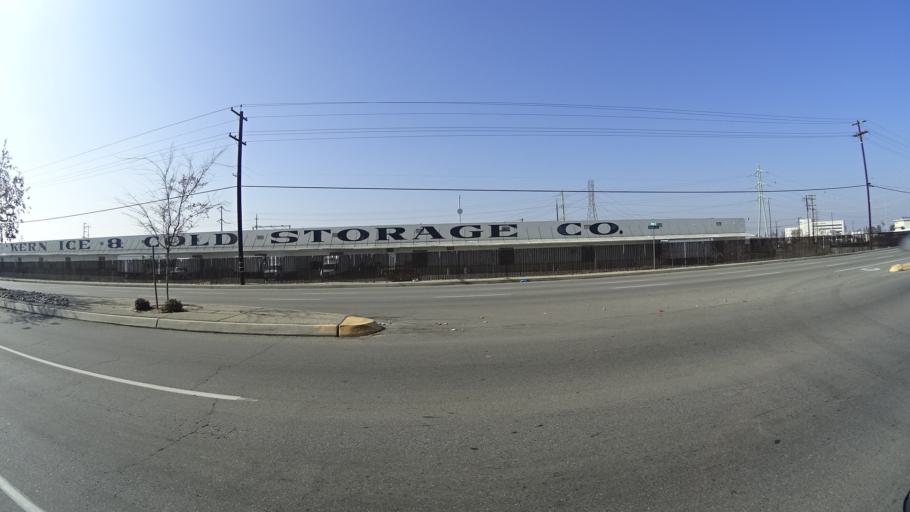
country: US
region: California
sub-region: Kern County
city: Bakersfield
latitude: 35.3875
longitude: -119.0026
